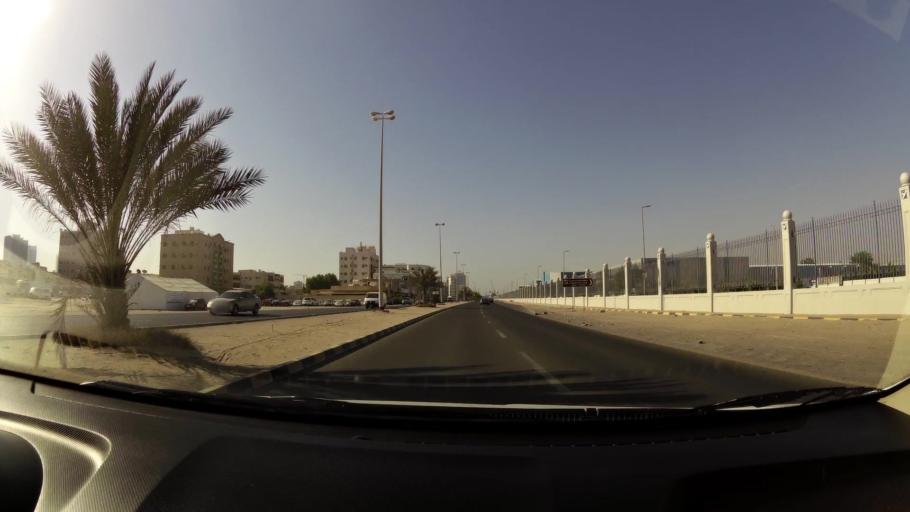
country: AE
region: Ajman
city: Ajman
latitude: 25.4077
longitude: 55.4518
